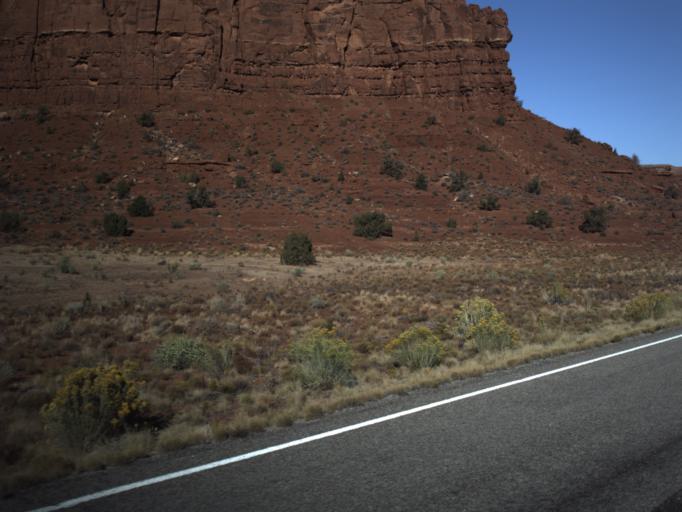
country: US
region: Utah
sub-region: San Juan County
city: Blanding
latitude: 37.6882
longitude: -110.2235
